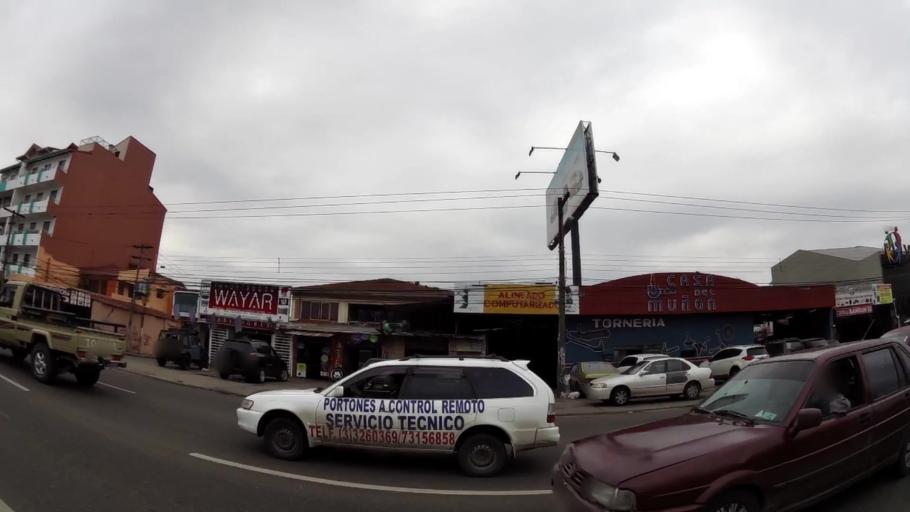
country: BO
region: Santa Cruz
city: Santa Cruz de la Sierra
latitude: -17.7724
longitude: -63.1672
